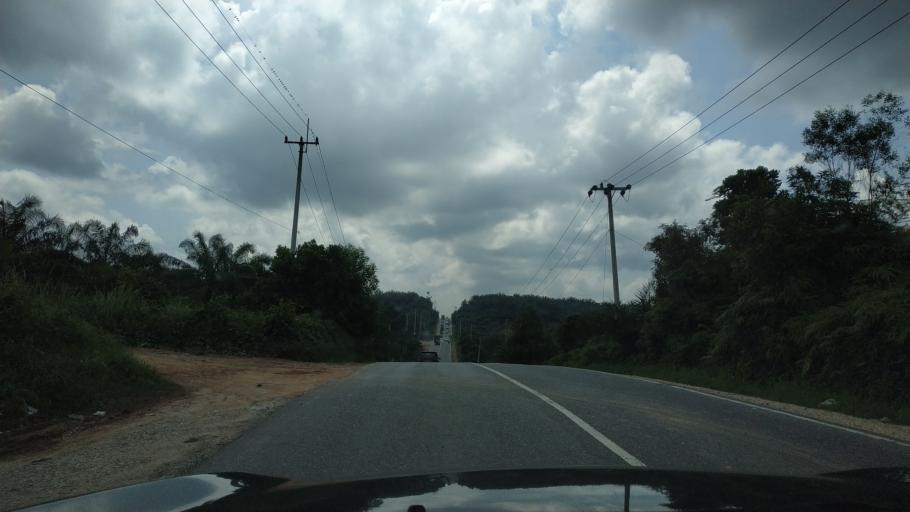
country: ID
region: Riau
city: Pangkalanbunut
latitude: 0.3016
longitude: 101.9163
